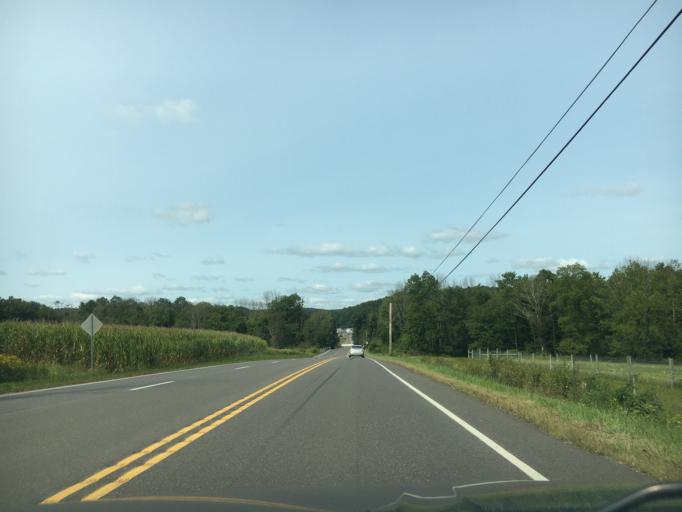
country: US
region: Pennsylvania
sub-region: Carbon County
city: Summit Hill
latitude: 40.7168
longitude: -75.8474
